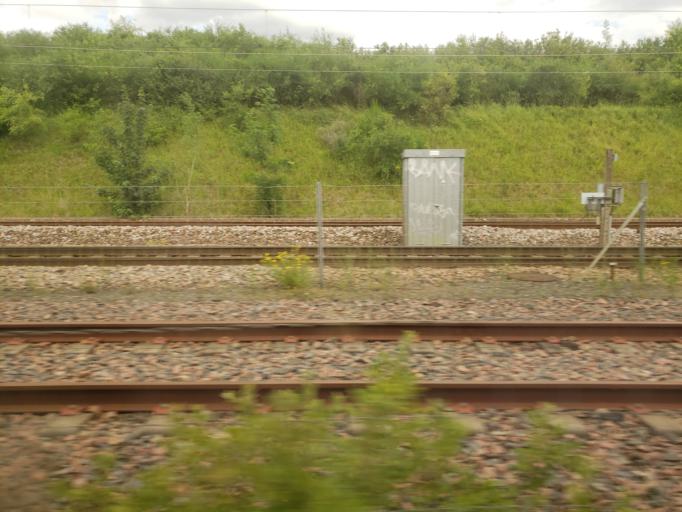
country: FR
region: Ile-de-France
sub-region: Departement de Seine-et-Marne
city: Serris
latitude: 48.8612
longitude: 2.7811
